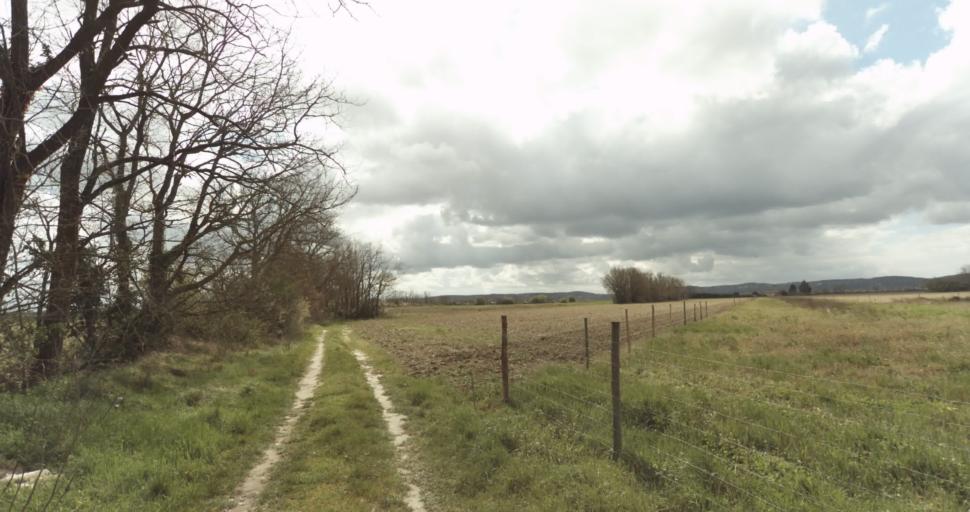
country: FR
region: Midi-Pyrenees
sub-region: Departement de la Haute-Garonne
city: Auterive
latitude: 43.3314
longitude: 1.4841
